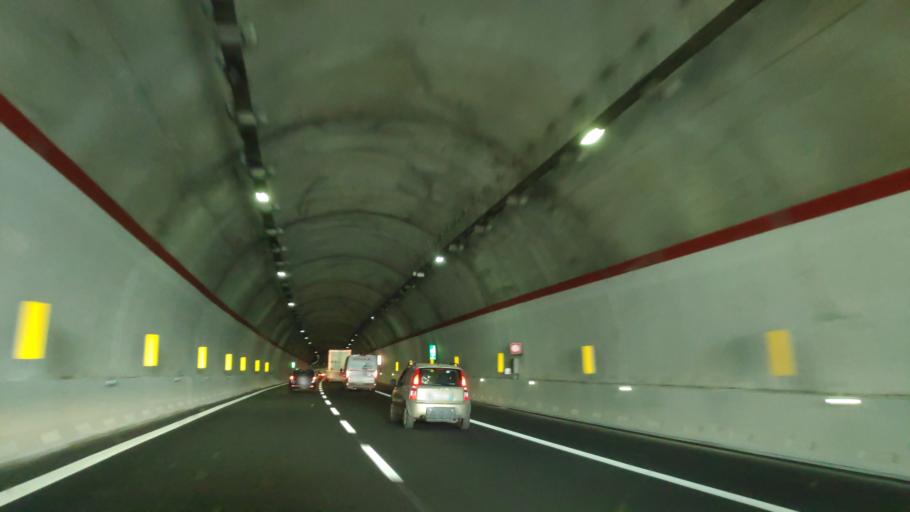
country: IT
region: Campania
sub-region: Provincia di Salerno
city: Casalbuono
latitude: 40.1874
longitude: 15.7080
